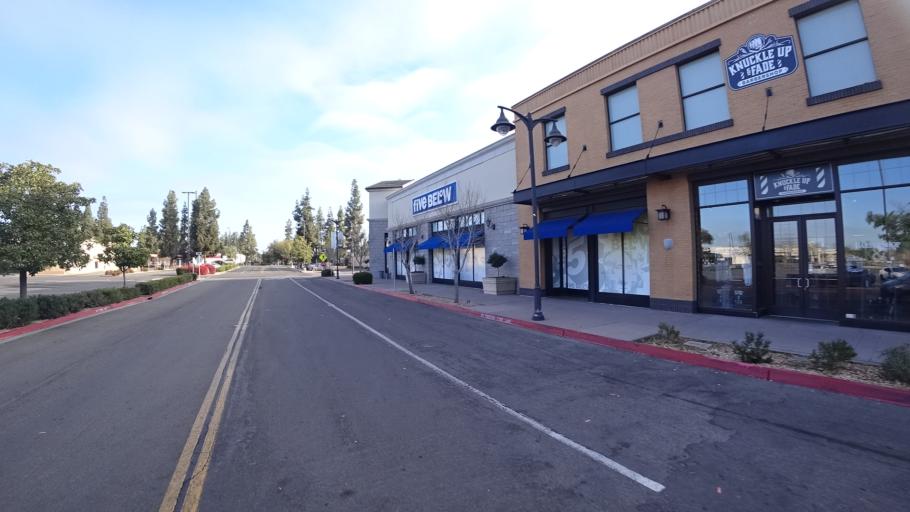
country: US
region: California
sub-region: Fresno County
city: Fresno
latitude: 36.8072
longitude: -119.7768
